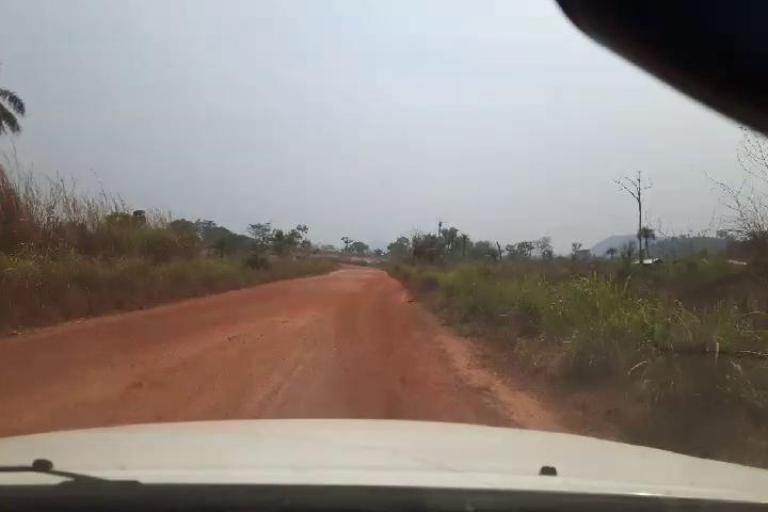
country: SL
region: Northern Province
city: Bumbuna
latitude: 9.0063
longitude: -11.7732
